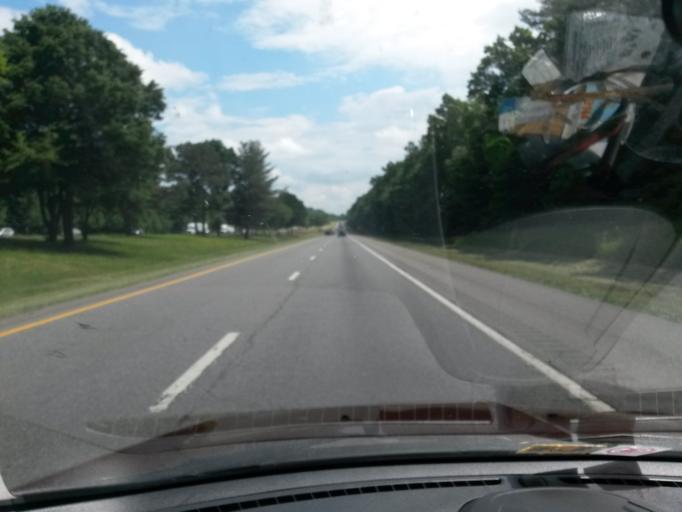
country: US
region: North Carolina
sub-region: Surry County
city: Dobson
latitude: 36.3395
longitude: -80.7947
